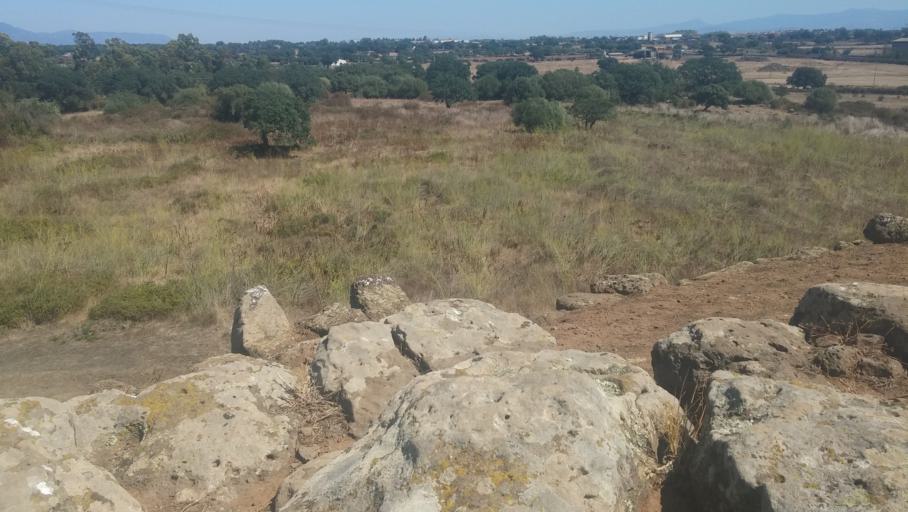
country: IT
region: Sardinia
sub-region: Provincia di Oristano
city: Abbasanta
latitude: 40.1169
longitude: 8.7903
